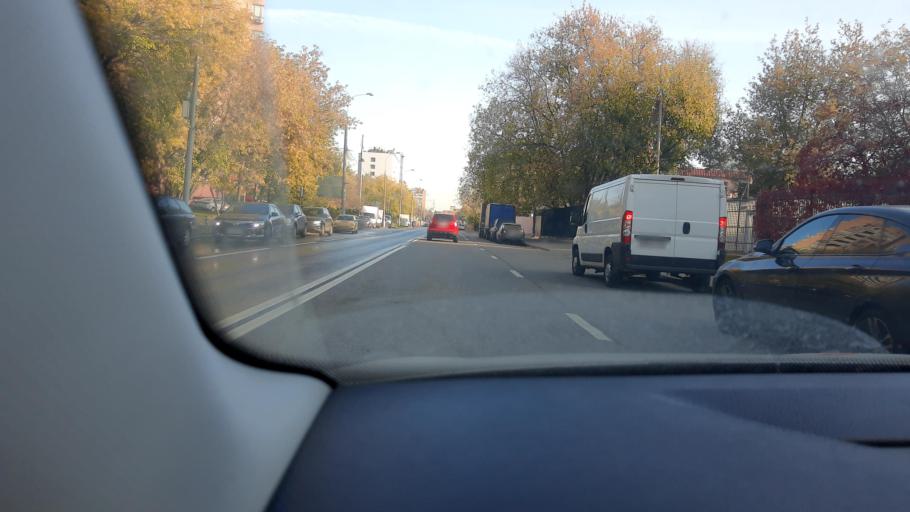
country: RU
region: Moscow
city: Kolomenskoye
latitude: 55.6777
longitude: 37.6887
